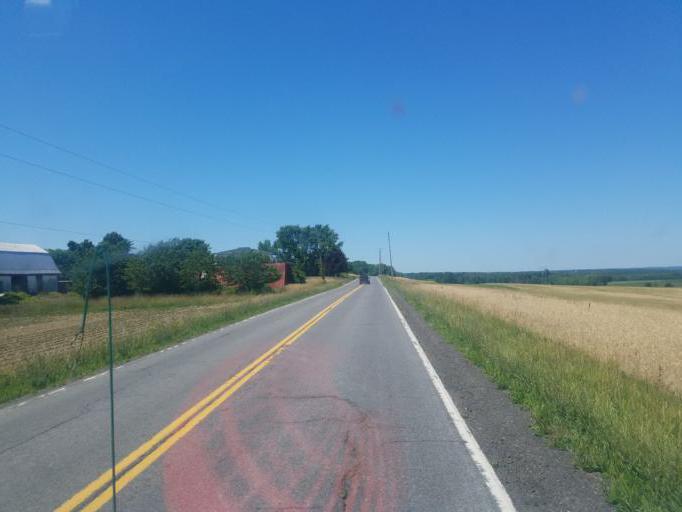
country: US
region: New York
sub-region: Yates County
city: Penn Yan
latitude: 42.7450
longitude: -77.0017
